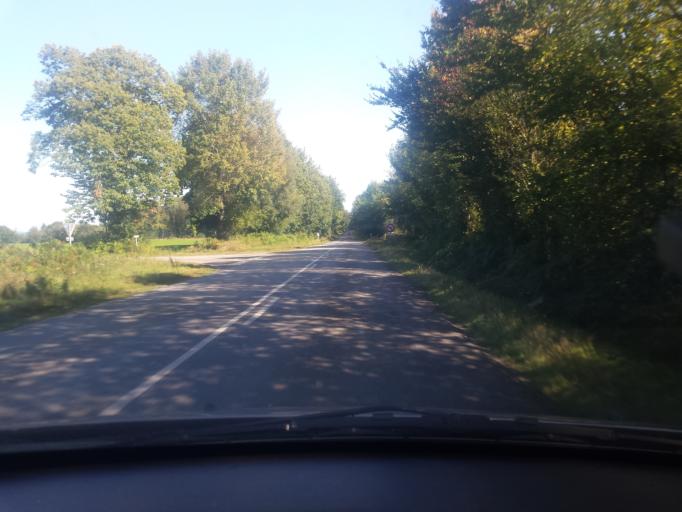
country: FR
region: Brittany
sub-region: Departement du Morbihan
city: Cleguerec
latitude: 48.1000
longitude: -3.0950
